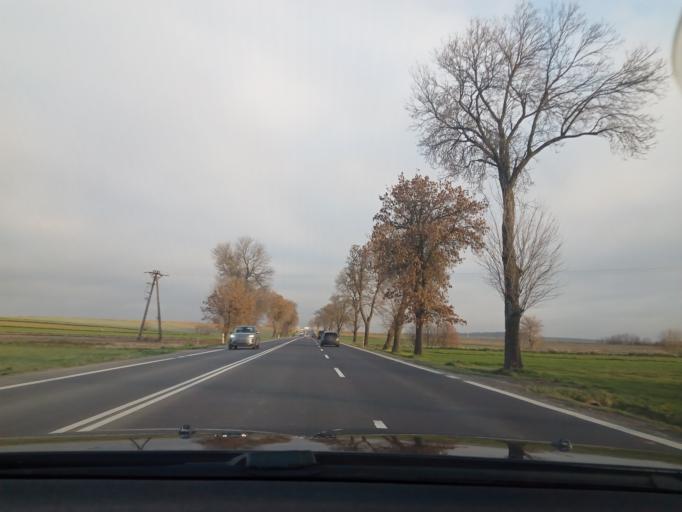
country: PL
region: Lesser Poland Voivodeship
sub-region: Powiat miechowski
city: Miechow
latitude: 50.3057
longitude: 20.0381
